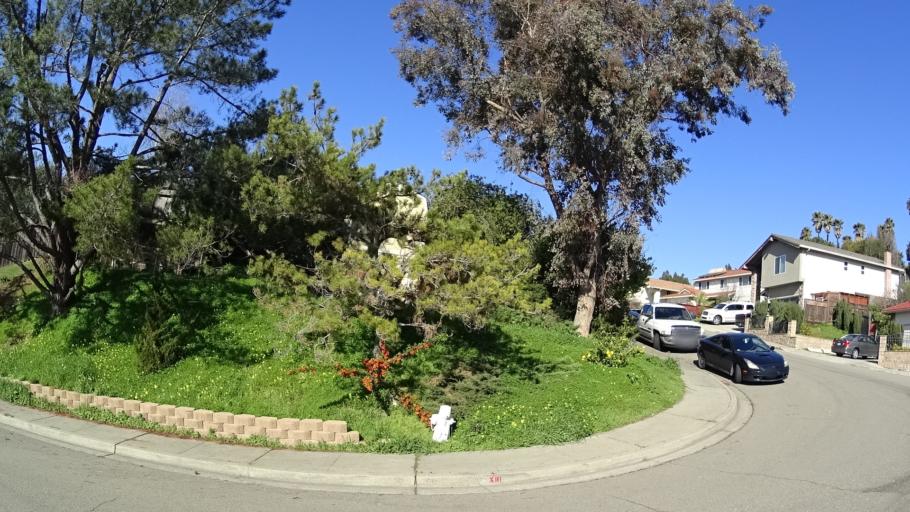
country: US
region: California
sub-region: Alameda County
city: Fairview
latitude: 37.6667
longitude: -122.0489
